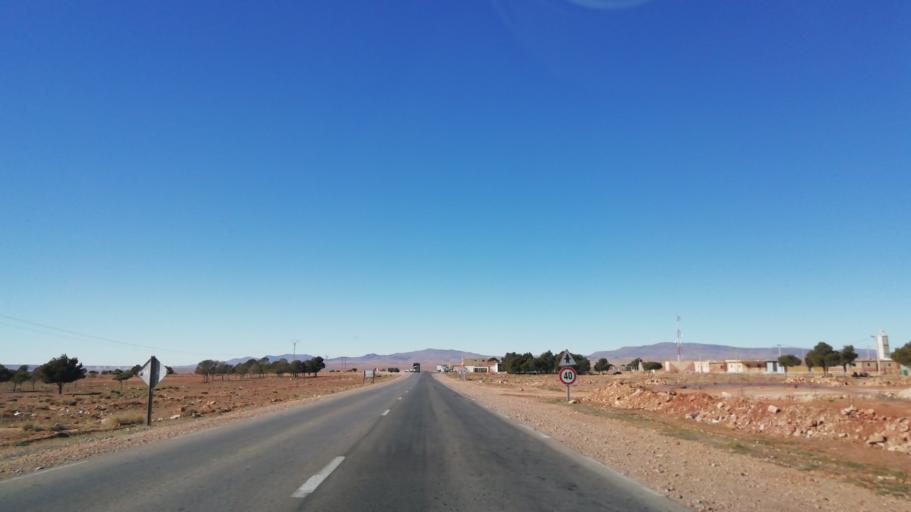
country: DZ
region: El Bayadh
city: El Bayadh
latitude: 33.6324
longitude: 1.3560
